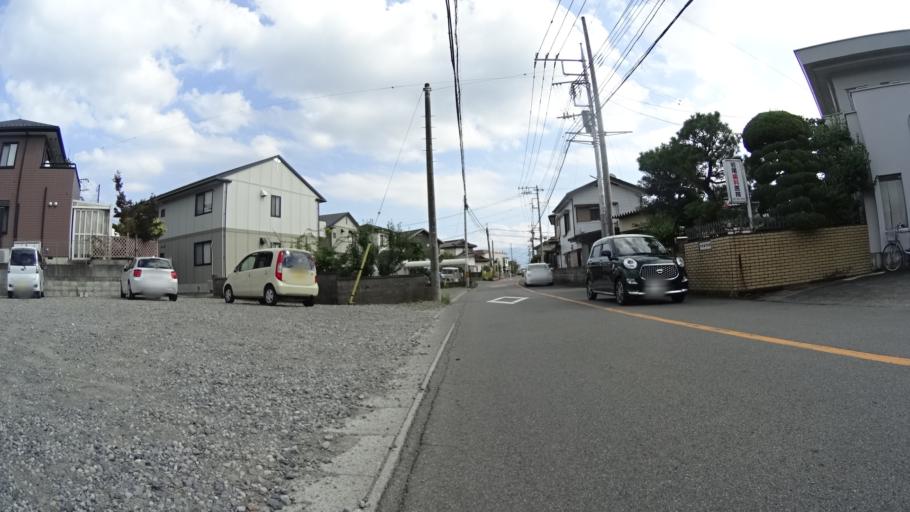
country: JP
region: Yamanashi
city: Kofu-shi
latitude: 35.6845
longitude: 138.5664
